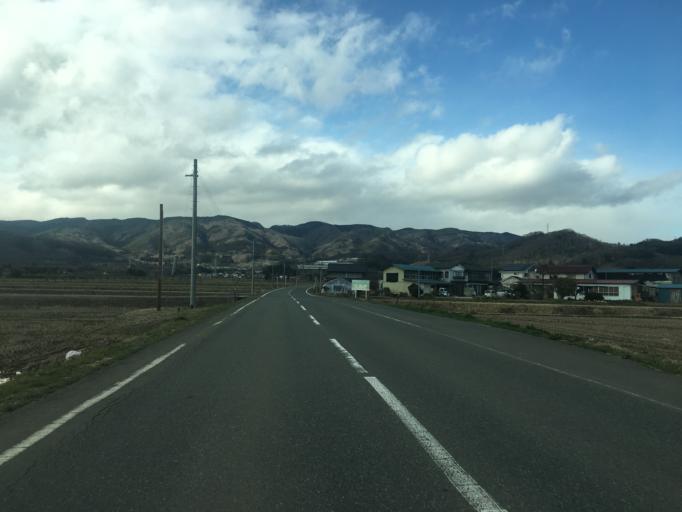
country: JP
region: Fukushima
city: Yanagawamachi-saiwaicho
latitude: 37.8807
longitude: 140.5931
